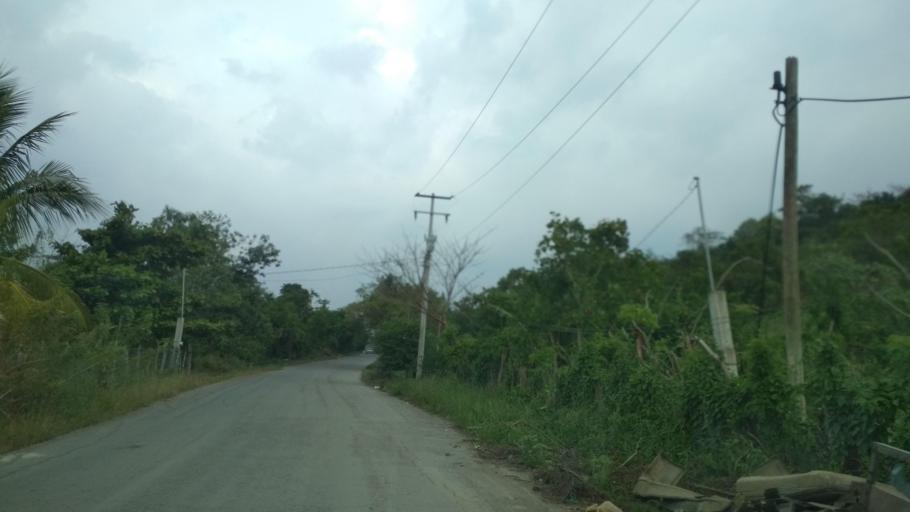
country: MM
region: Kayah
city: Loikaw
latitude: 20.2411
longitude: 97.2747
